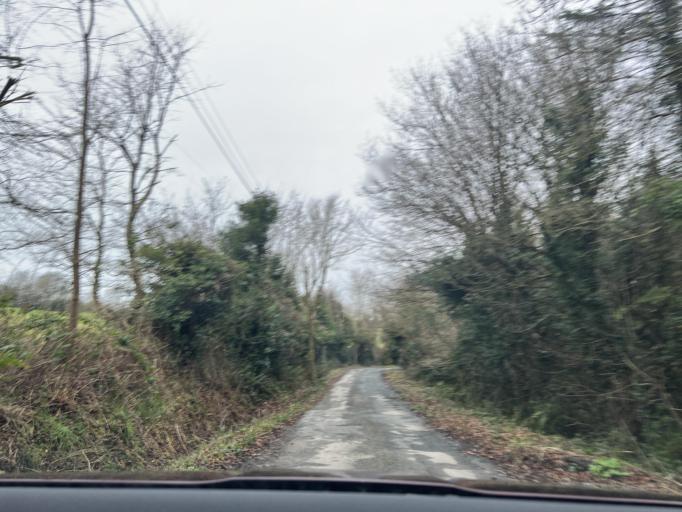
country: IE
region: Leinster
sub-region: Loch Garman
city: Castlebridge
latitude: 52.3849
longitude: -6.5523
